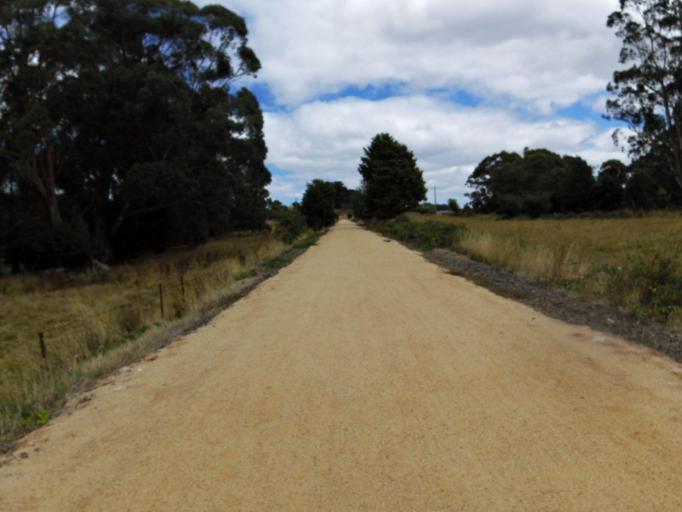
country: AU
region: Victoria
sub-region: Bass Coast
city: North Wonthaggi
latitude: -38.4340
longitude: 145.8351
